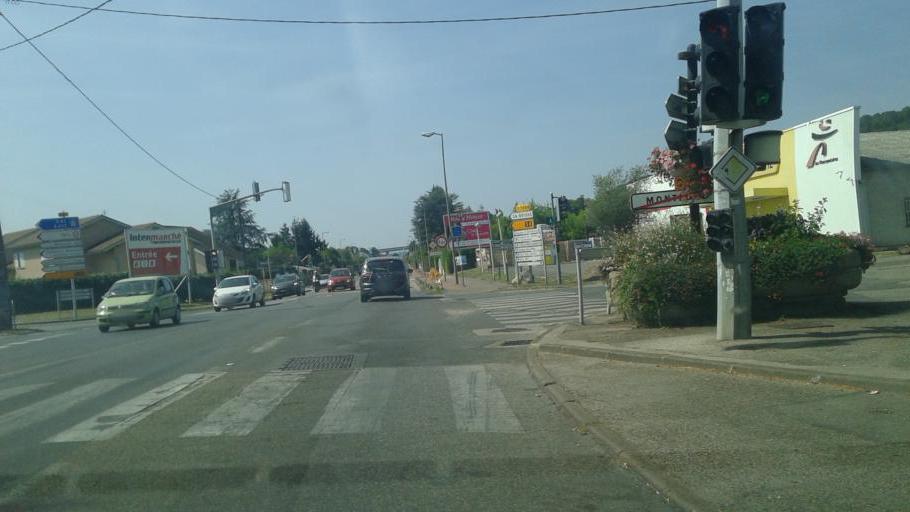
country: FR
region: Rhone-Alpes
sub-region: Departement de l'Ain
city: Montluel
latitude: 45.8483
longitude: 5.0474
